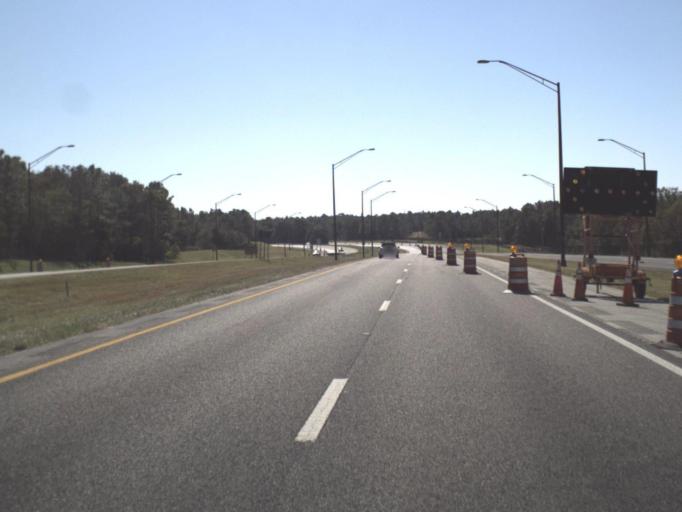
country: US
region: Florida
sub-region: Citrus County
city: Sugarmill Woods
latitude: 28.6541
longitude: -82.4936
